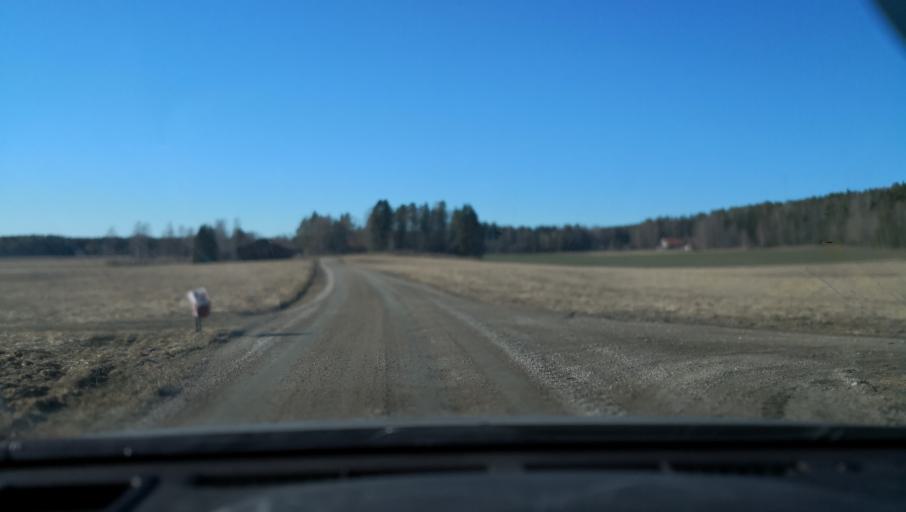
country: SE
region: Vaestmanland
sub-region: Sala Kommun
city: Sala
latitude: 60.1491
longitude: 16.6403
